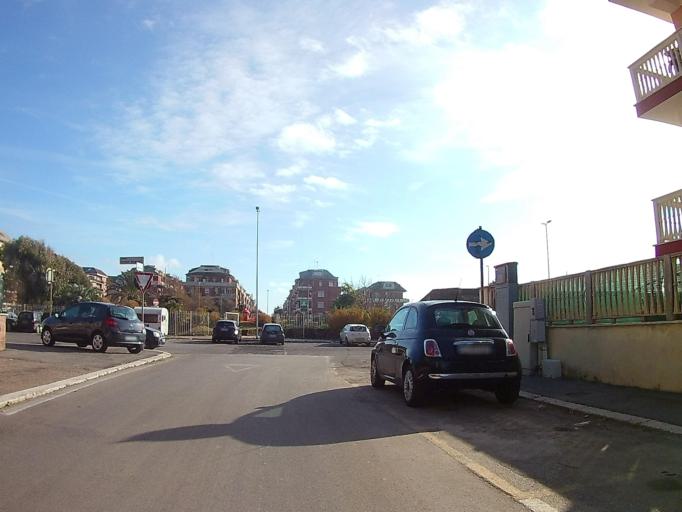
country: IT
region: Latium
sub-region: Citta metropolitana di Roma Capitale
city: Lido di Ostia
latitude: 41.7369
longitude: 12.2558
